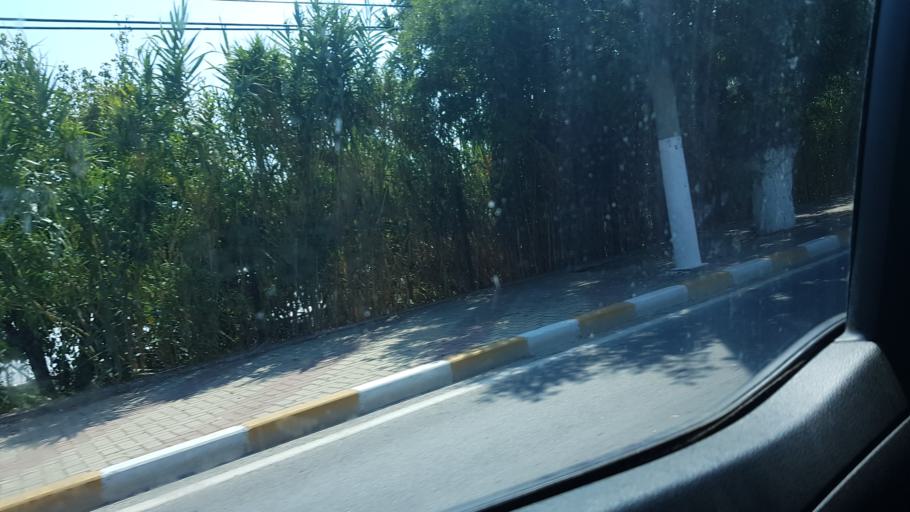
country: TR
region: Izmir
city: Urla
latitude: 38.3413
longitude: 26.7702
